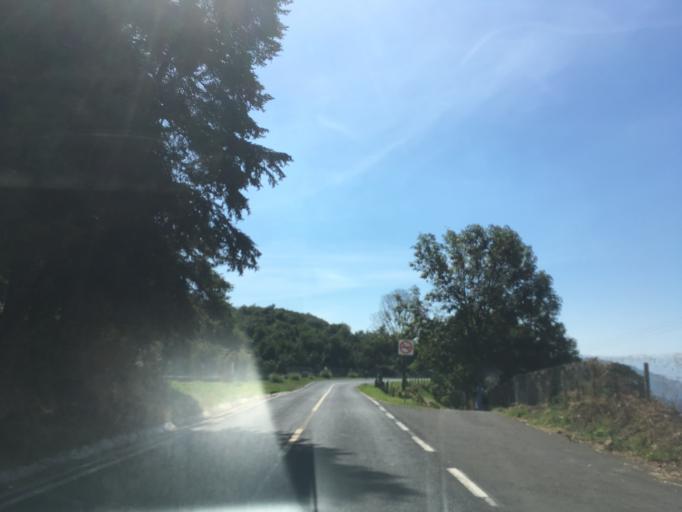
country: MX
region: Michoacan
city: Tzitzio
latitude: 19.6538
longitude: -100.9344
